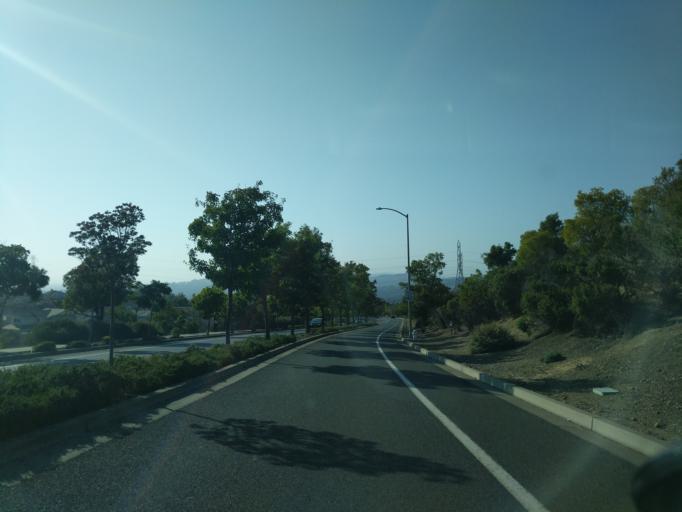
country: US
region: California
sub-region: Alameda County
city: Fairview
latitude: 37.6787
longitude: -122.0313
